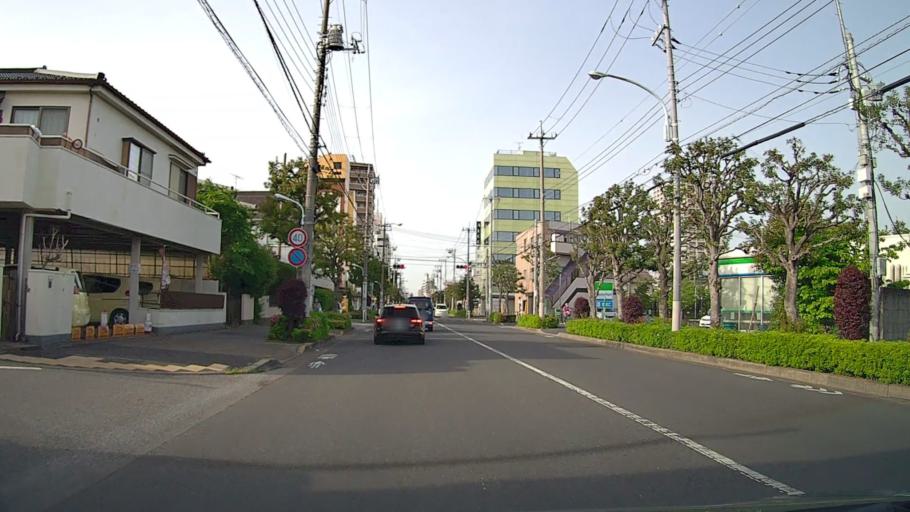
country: JP
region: Saitama
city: Soka
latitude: 35.7898
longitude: 139.7865
